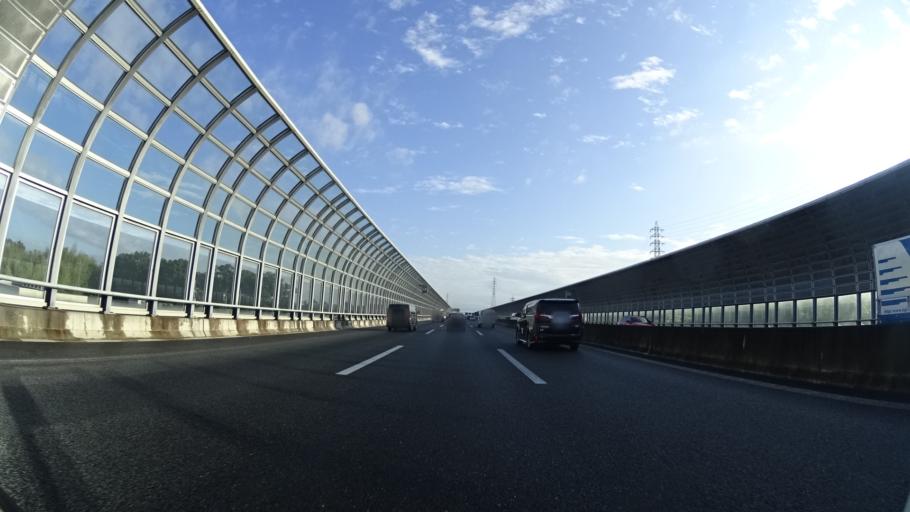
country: JP
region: Osaka
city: Neyagawa
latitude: 34.7672
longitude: 135.6547
